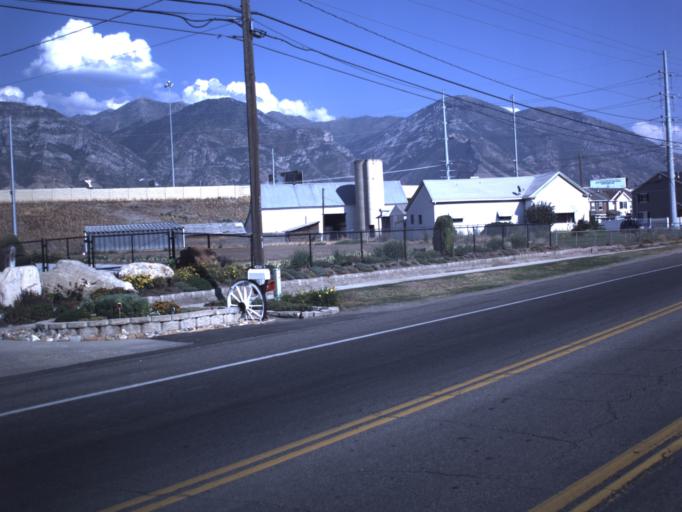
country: US
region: Utah
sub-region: Utah County
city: Provo
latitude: 40.2452
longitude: -111.6978
